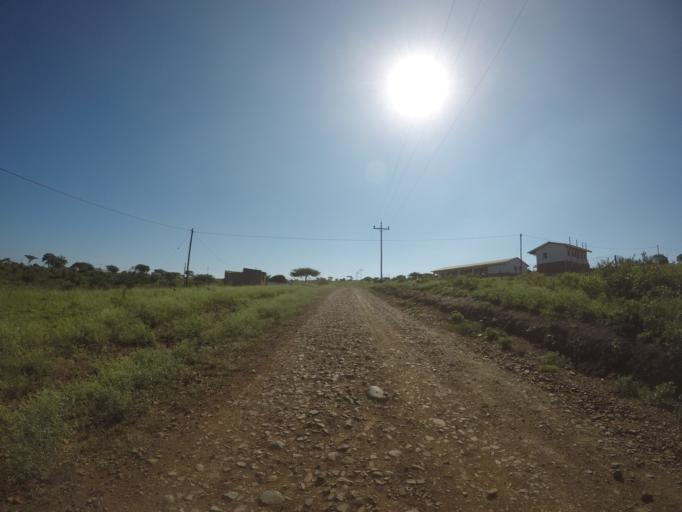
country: ZA
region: KwaZulu-Natal
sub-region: uThungulu District Municipality
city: Empangeni
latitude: -28.5714
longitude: 31.7204
